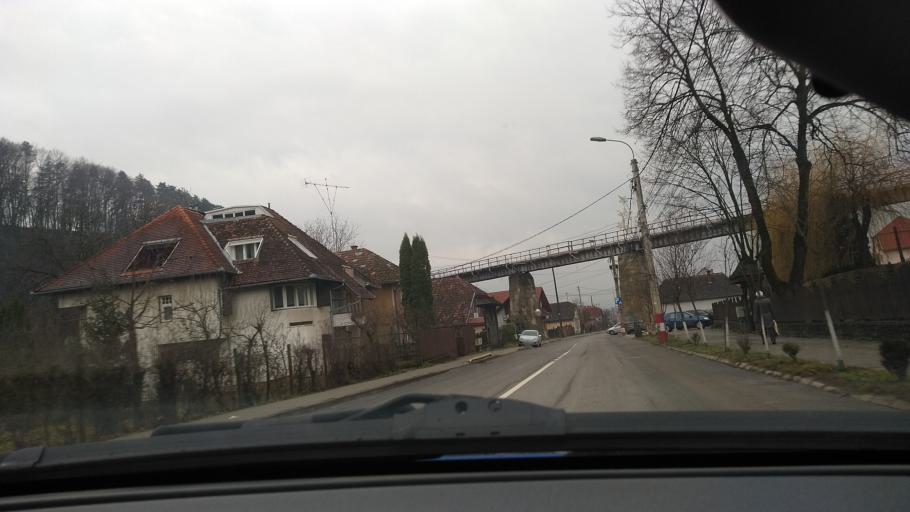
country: RO
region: Mures
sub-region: Oras Sovata
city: Sovata
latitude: 46.5911
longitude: 25.0715
